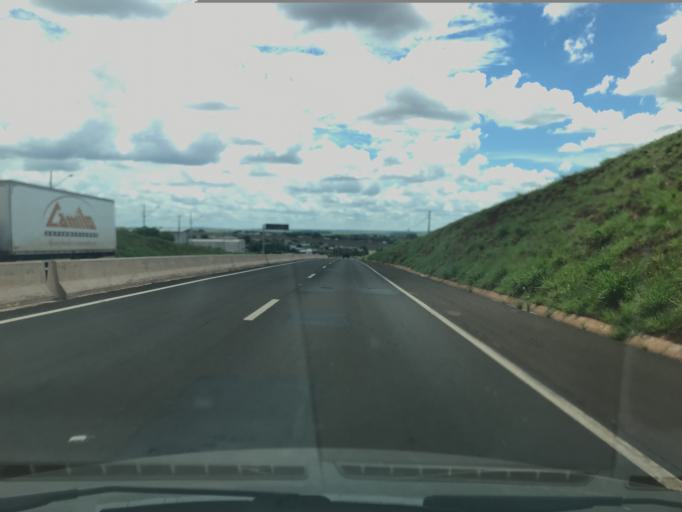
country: BR
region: Parana
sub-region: Maringa
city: Maringa
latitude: -23.3745
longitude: -51.9198
